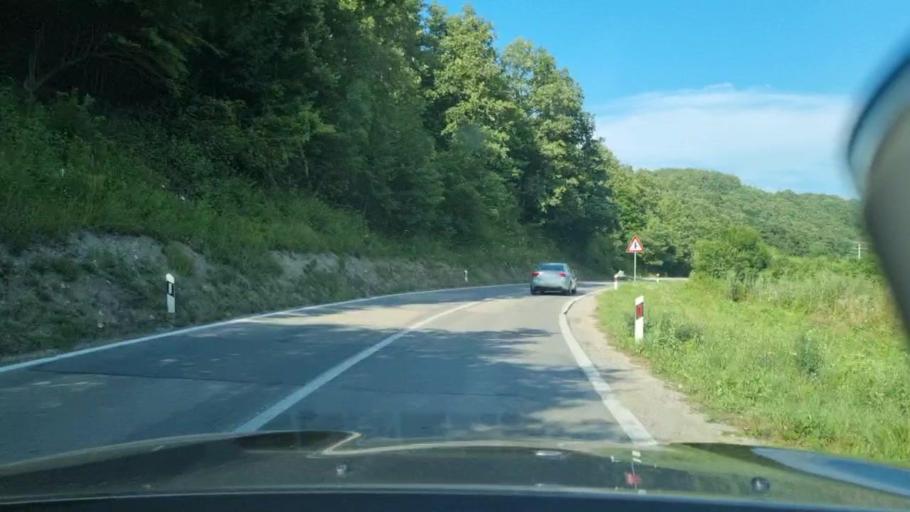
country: BA
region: Federation of Bosnia and Herzegovina
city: Coralici
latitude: 44.9998
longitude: 15.9040
